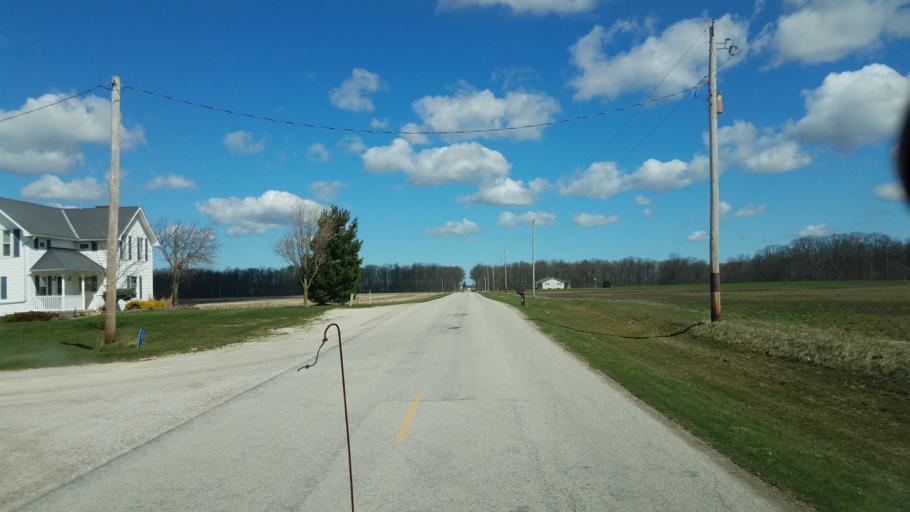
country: US
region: Ohio
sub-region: Sandusky County
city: Mount Carmel
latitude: 41.1776
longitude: -82.9380
